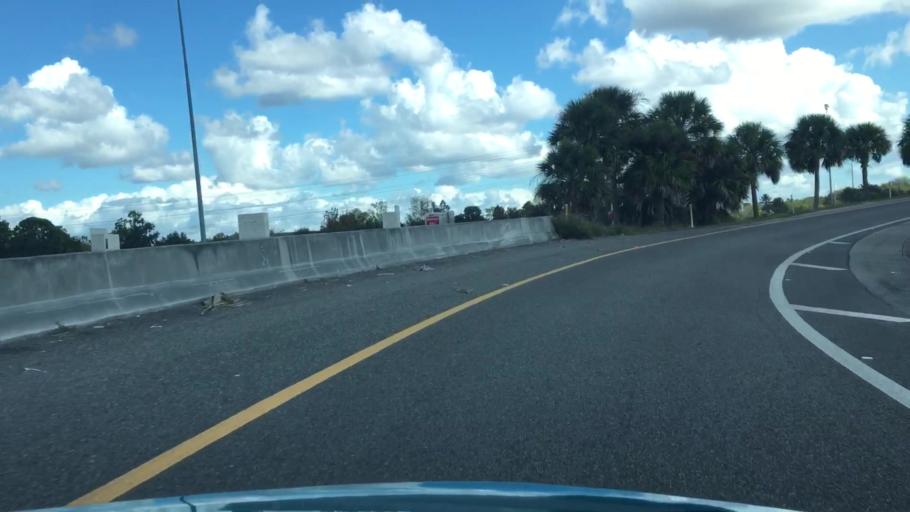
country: US
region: Florida
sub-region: Seminole County
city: Lake Mary
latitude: 28.8001
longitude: -81.3293
